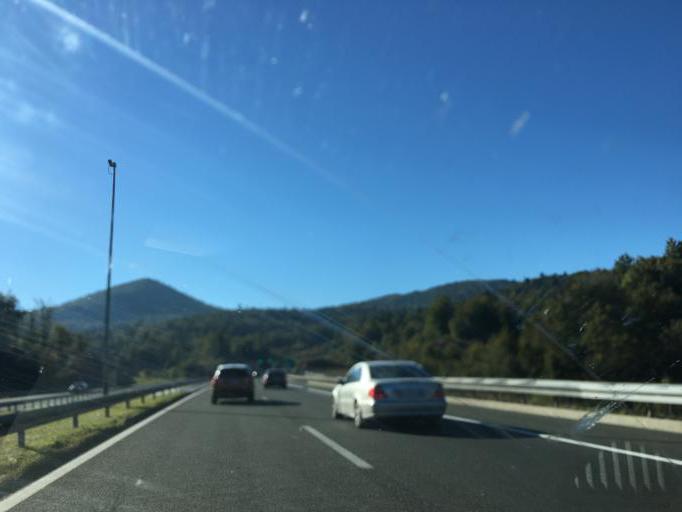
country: HR
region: Karlovacka
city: Ostarije
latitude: 45.1198
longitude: 15.2452
